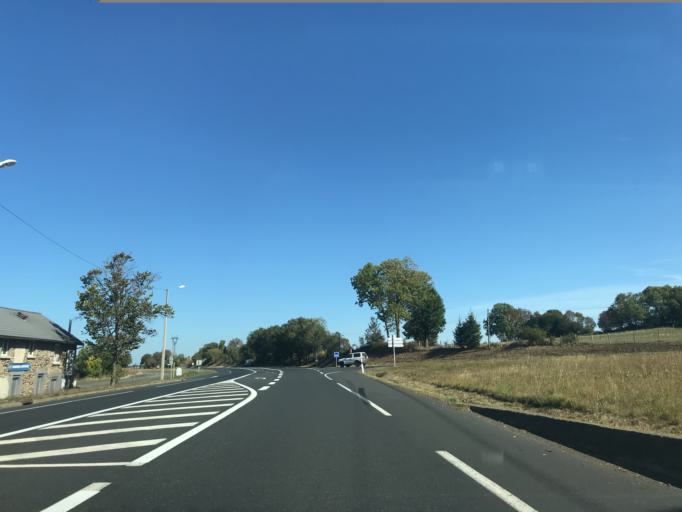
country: FR
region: Auvergne
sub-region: Departement du Puy-de-Dome
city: Gelles
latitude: 45.7029
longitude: 2.8091
